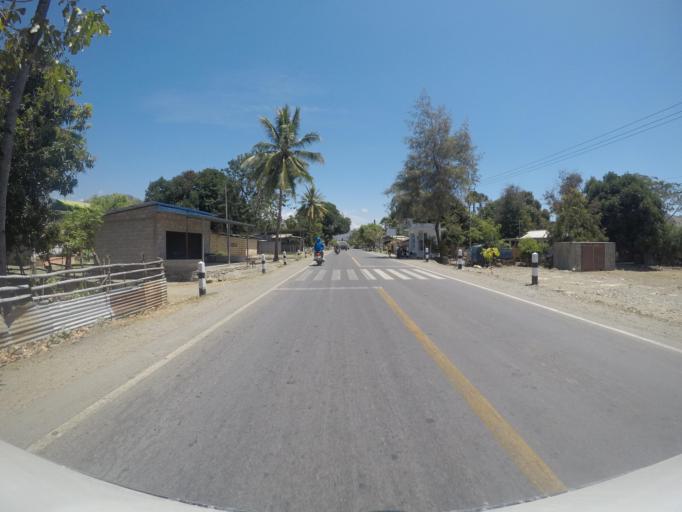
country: ID
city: Metinaro
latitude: -8.5392
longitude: 125.6821
